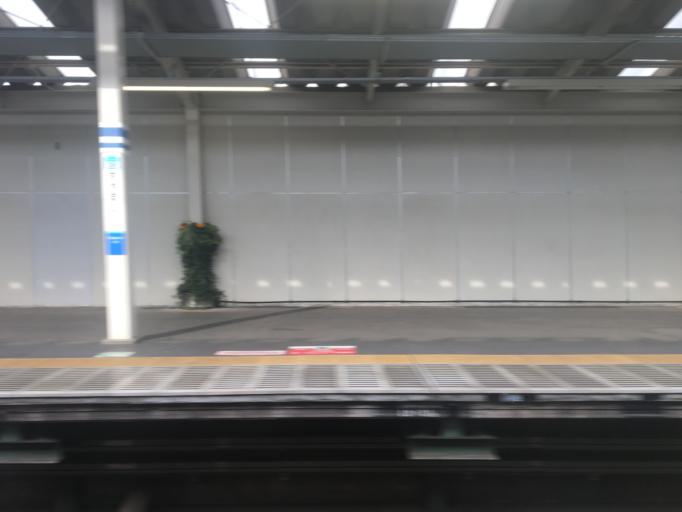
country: JP
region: Saitama
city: Sayama
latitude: 35.8578
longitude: 139.4135
